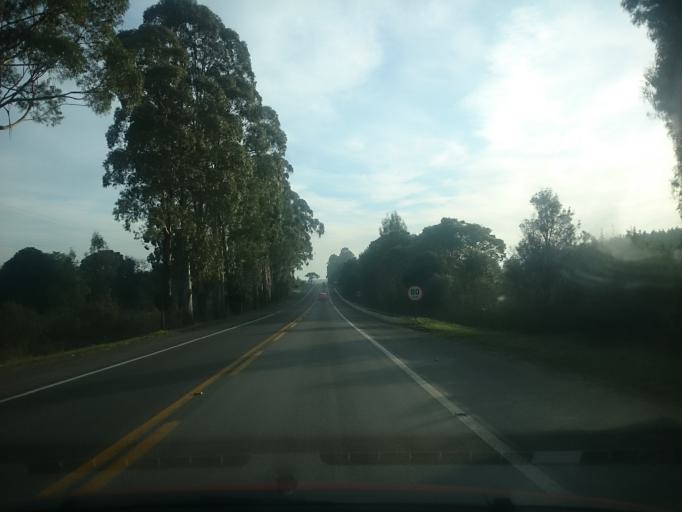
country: BR
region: Rio Grande do Sul
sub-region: Vacaria
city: Estrela
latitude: -28.2623
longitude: -50.7855
